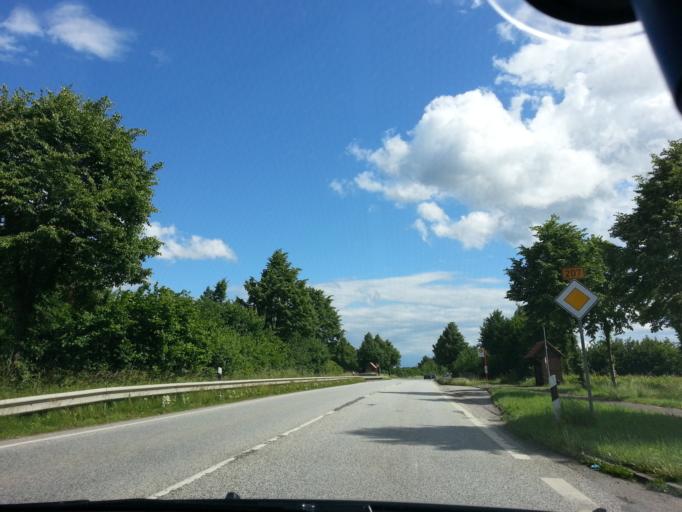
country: DE
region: Schleswig-Holstein
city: Buchholz
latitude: 53.7337
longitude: 10.7364
